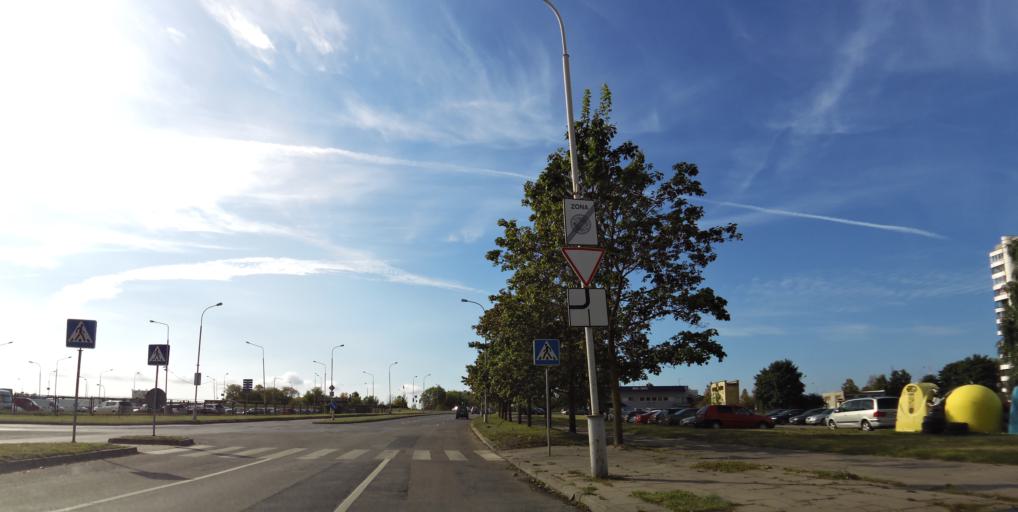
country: LT
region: Vilnius County
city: Seskine
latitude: 54.7117
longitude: 25.2488
